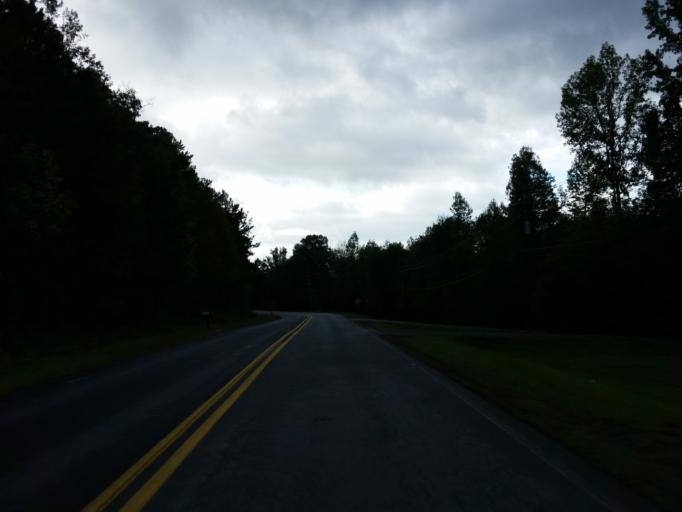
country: US
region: Georgia
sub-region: Bartow County
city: Emerson
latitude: 34.1162
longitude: -84.7959
